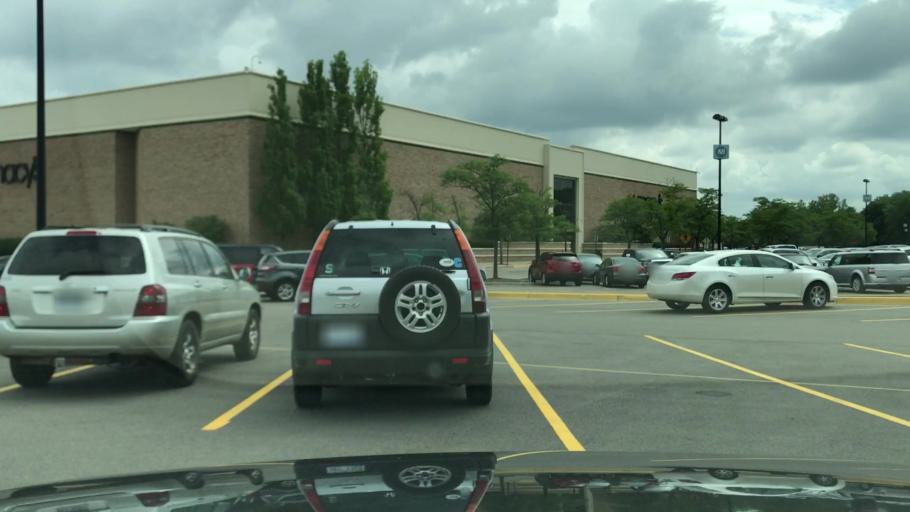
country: US
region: Michigan
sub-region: Kent County
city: East Grand Rapids
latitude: 42.9185
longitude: -85.5892
